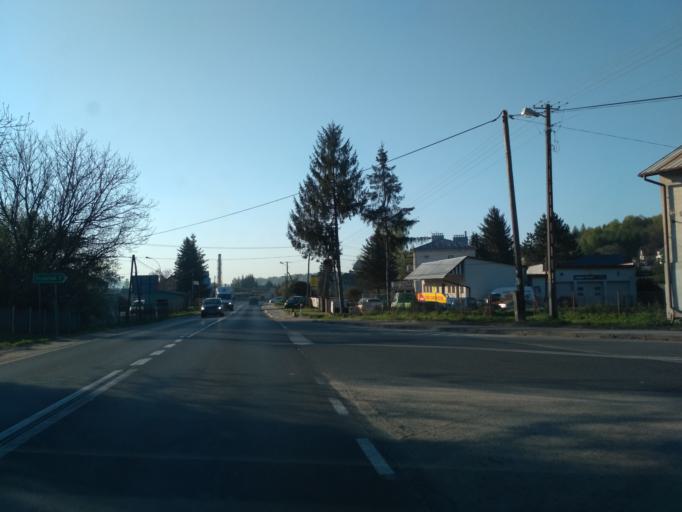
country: PL
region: Subcarpathian Voivodeship
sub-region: Powiat strzyzowski
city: Frysztak
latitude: 49.8312
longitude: 21.6161
